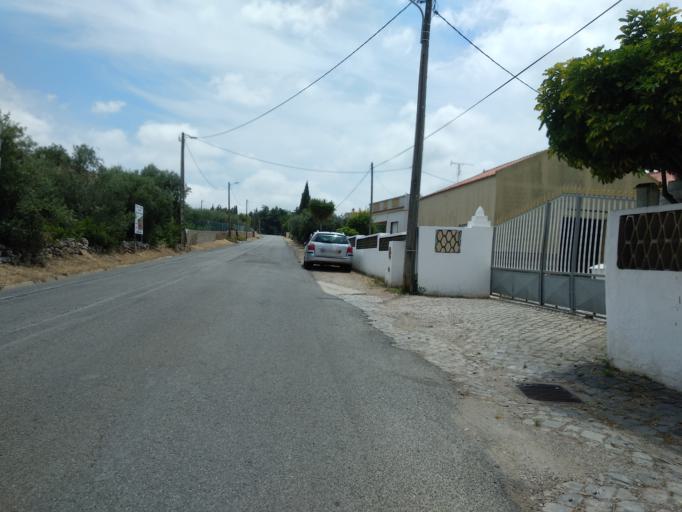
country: PT
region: Faro
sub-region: Sao Bras de Alportel
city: Sao Bras de Alportel
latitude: 37.1657
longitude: -7.8923
